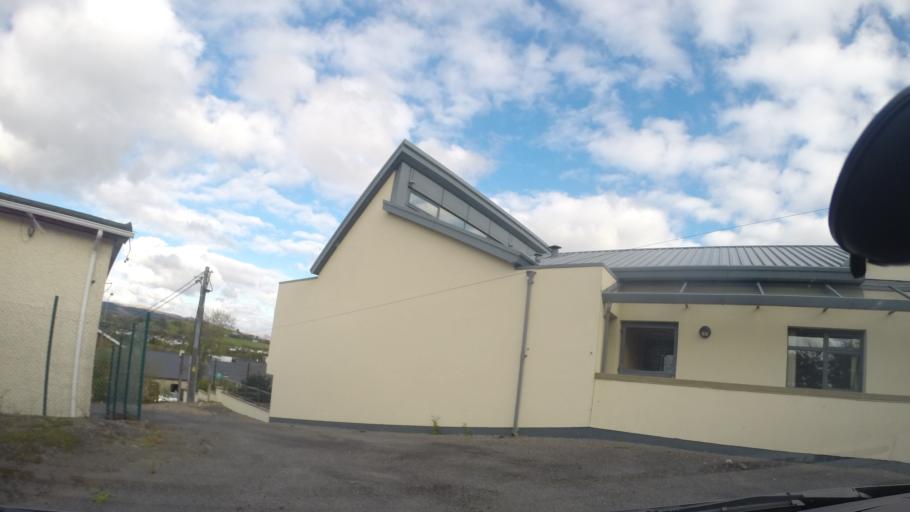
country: IE
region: Ulster
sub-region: County Donegal
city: Donegal
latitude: 54.6544
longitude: -8.1043
